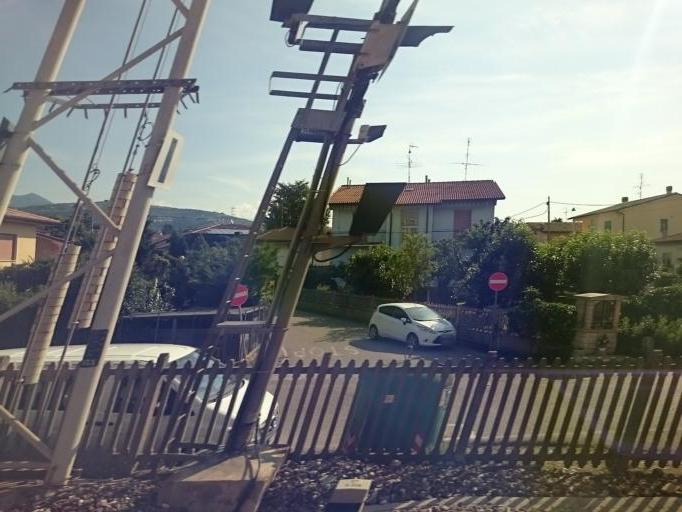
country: IT
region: Veneto
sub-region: Provincia di Verona
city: Sant'Ambrogio di Valpollicella
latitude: 45.5136
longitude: 10.8259
